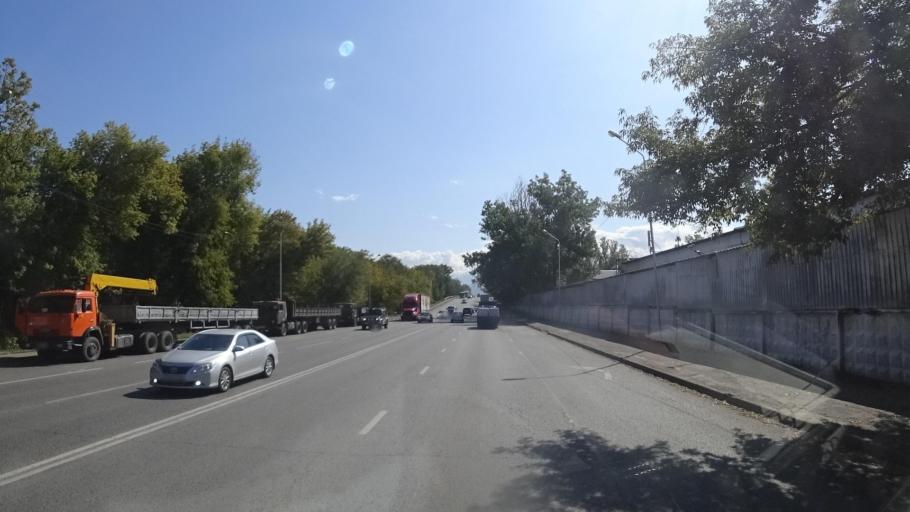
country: KZ
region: Almaty Oblysy
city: Pervomayskiy
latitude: 43.3439
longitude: 76.9739
